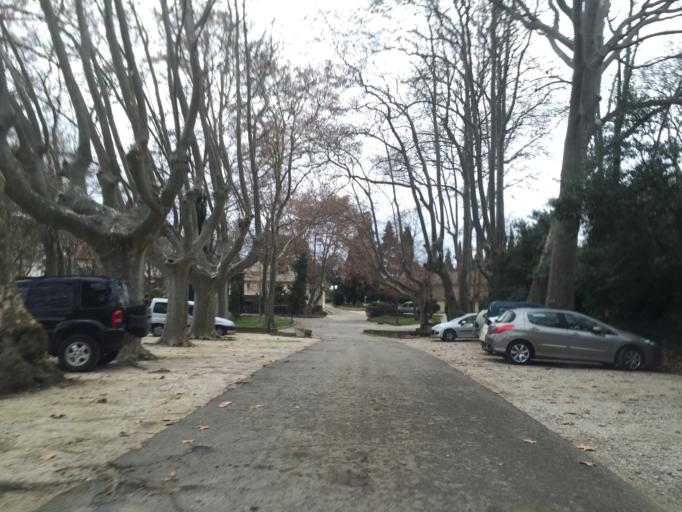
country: FR
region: Provence-Alpes-Cote d'Azur
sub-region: Departement du Vaucluse
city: Chateauneuf-du-Pape
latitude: 44.0486
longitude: 4.8589
